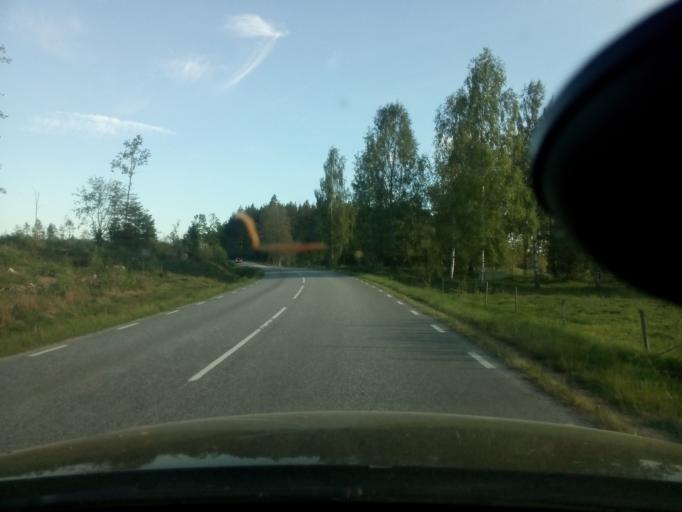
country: SE
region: Soedermanland
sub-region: Nykopings Kommun
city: Nykoping
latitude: 58.7856
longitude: 17.0038
